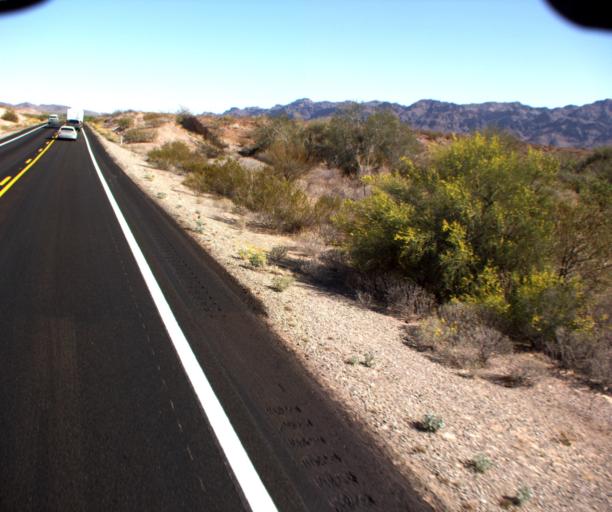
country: US
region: Arizona
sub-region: Yuma County
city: Wellton
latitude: 33.1588
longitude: -114.2803
